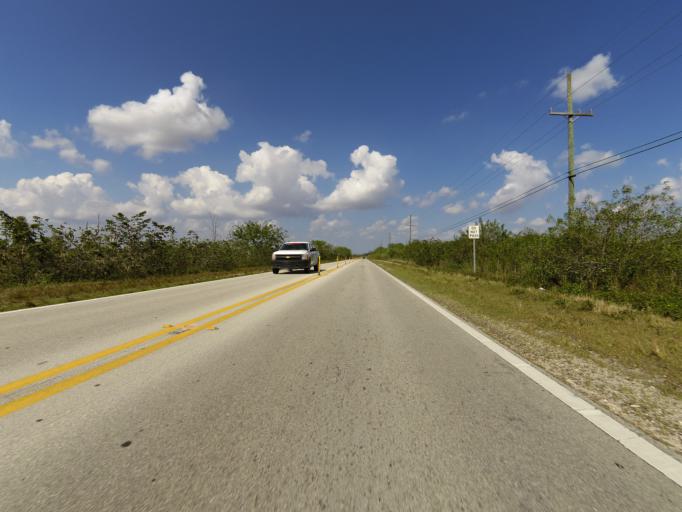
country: US
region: Florida
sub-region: Miami-Dade County
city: Palm Springs North
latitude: 25.9355
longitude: -80.4450
